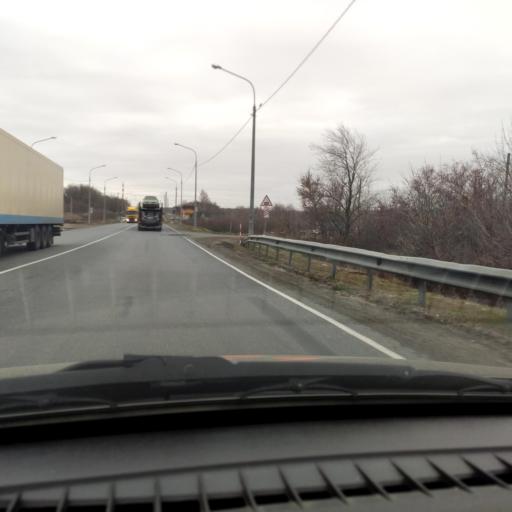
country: RU
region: Samara
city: Zhigulevsk
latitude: 53.3668
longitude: 49.4574
